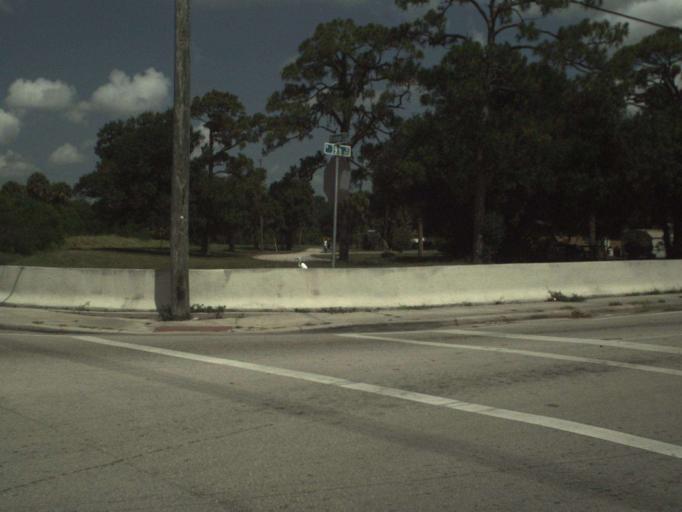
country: US
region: Florida
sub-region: Saint Lucie County
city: Fort Pierce North
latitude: 27.4476
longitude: -80.3641
